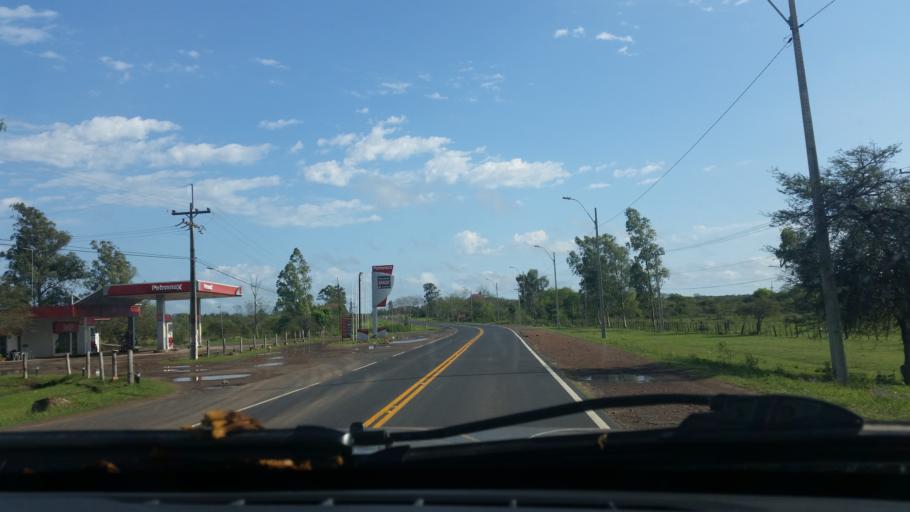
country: PY
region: Presidente Hayes
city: Villa Hayes
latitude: -25.0573
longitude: -57.5358
